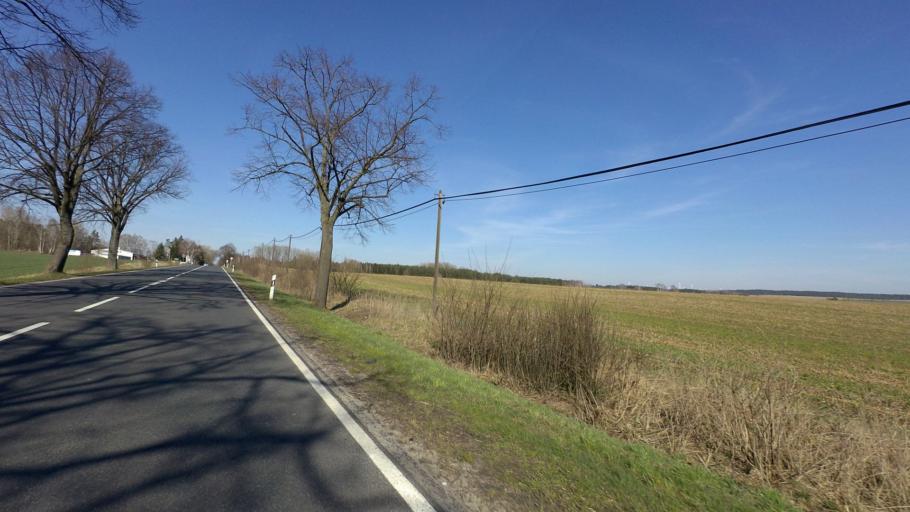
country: DE
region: Brandenburg
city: Angermunde
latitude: 52.9879
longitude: 13.9788
